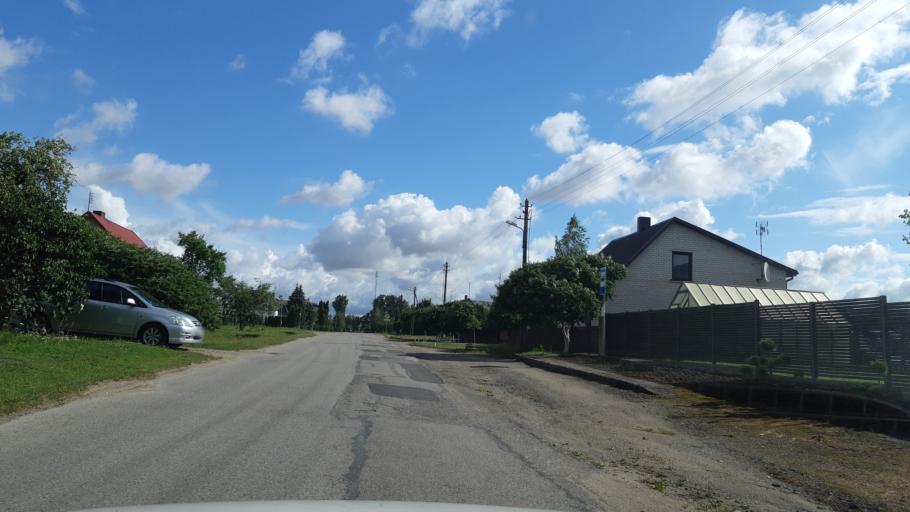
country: LT
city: Vilkaviskis
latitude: 54.6379
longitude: 23.0545
